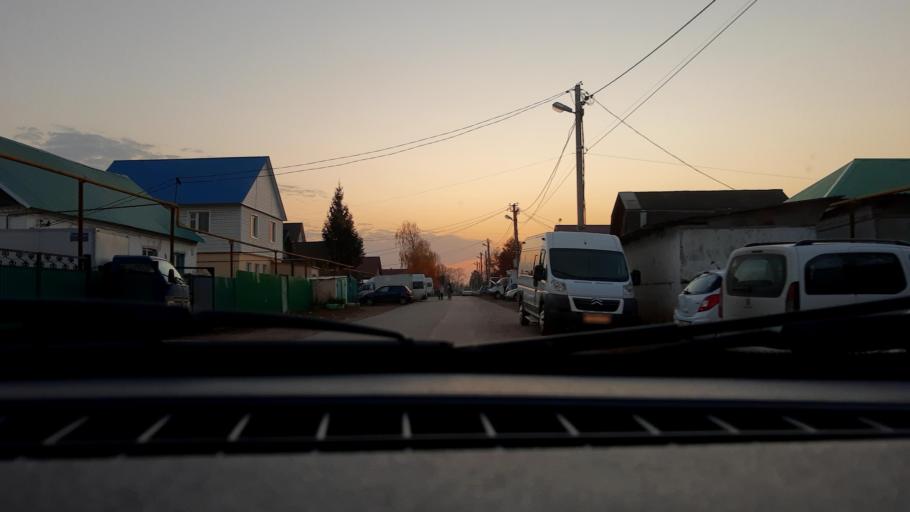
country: RU
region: Bashkortostan
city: Mikhaylovka
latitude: 54.7620
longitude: 55.9129
